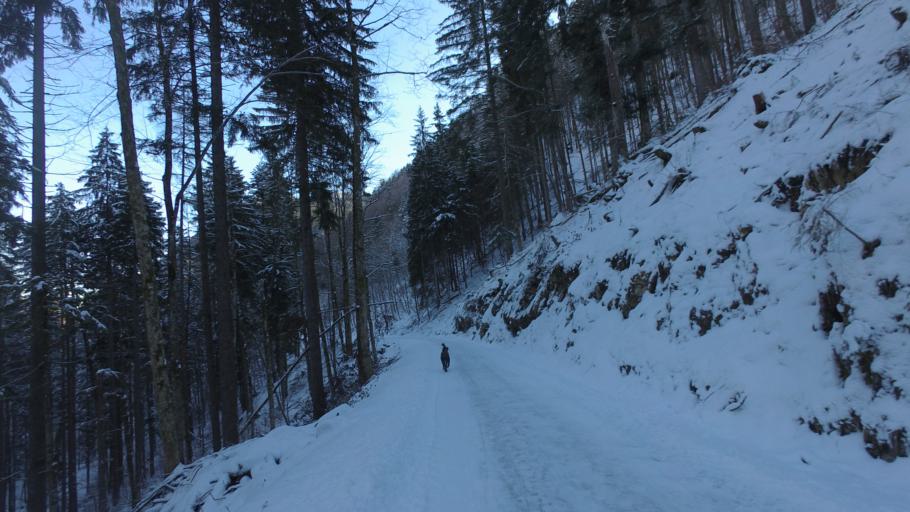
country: DE
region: Bavaria
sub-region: Upper Bavaria
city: Unterwossen
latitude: 47.7194
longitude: 12.5581
